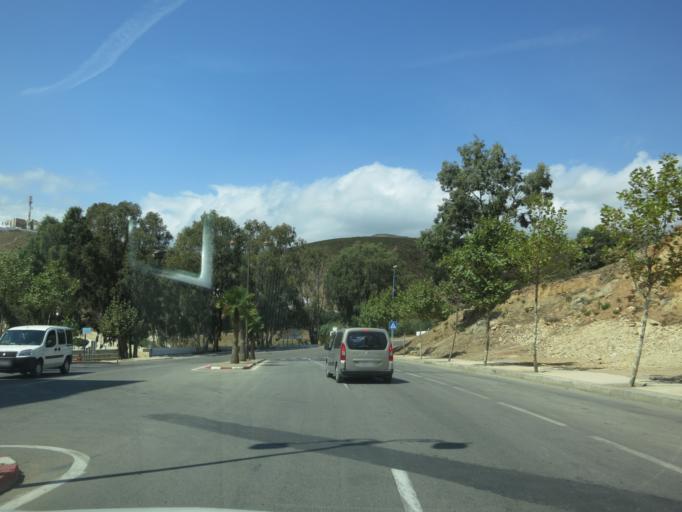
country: ES
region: Ceuta
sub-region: Ceuta
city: Ceuta
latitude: 35.8566
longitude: -5.3554
